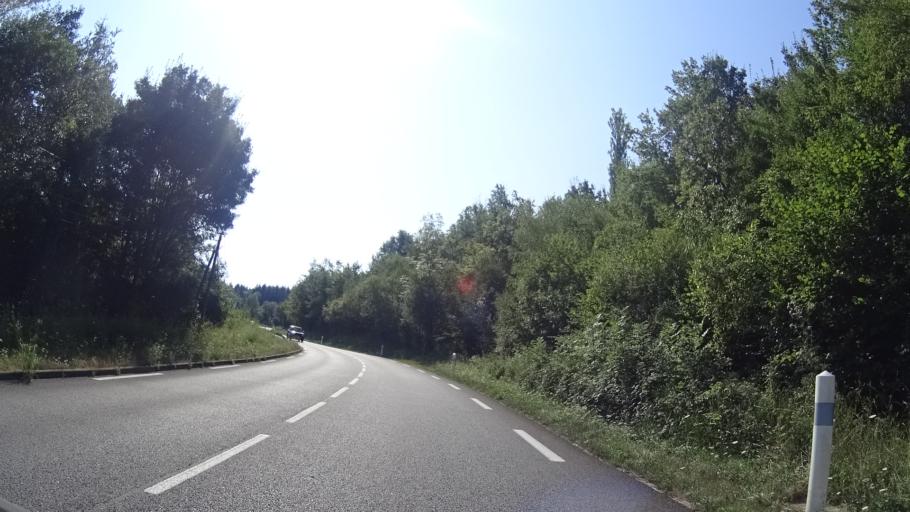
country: FR
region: Midi-Pyrenees
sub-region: Departement de l'Ariege
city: Lavelanet
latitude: 42.9207
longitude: 1.7525
